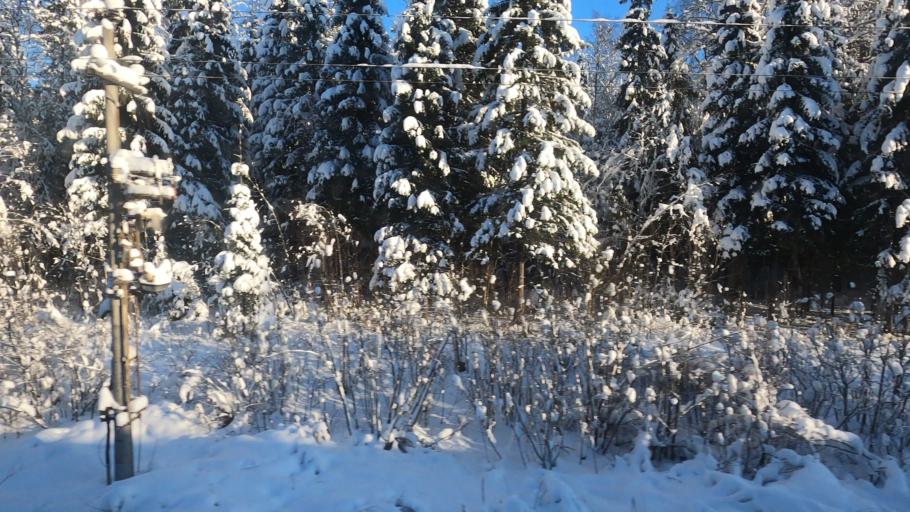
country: RU
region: Moskovskaya
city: Novo-Nikol'skoye
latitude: 56.6212
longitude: 37.5654
